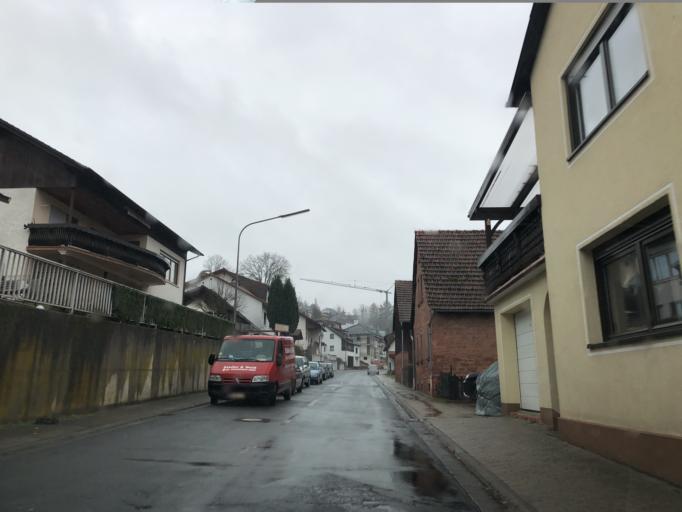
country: DE
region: Hesse
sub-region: Regierungsbezirk Darmstadt
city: Lutzelbach
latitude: 49.7693
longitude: 9.1051
